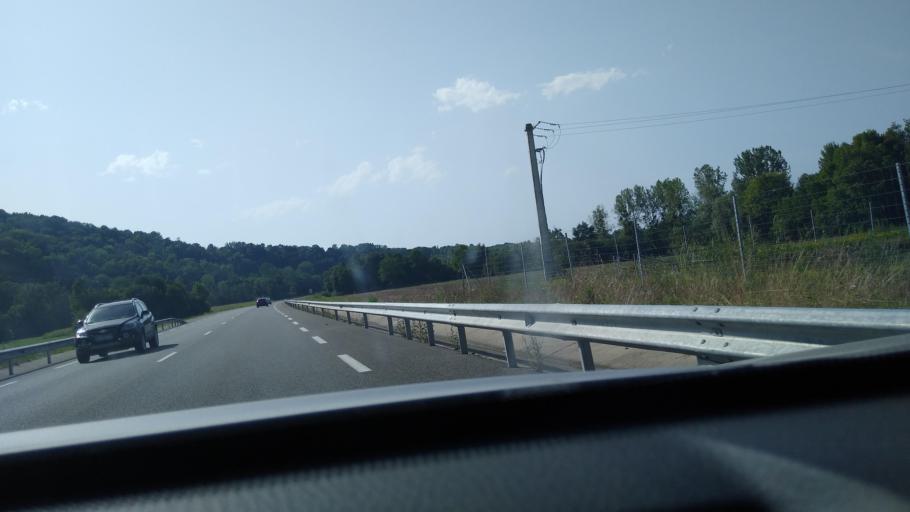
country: FR
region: Midi-Pyrenees
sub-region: Departement de la Haute-Garonne
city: Salies-du-Salat
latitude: 43.0340
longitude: 1.0040
